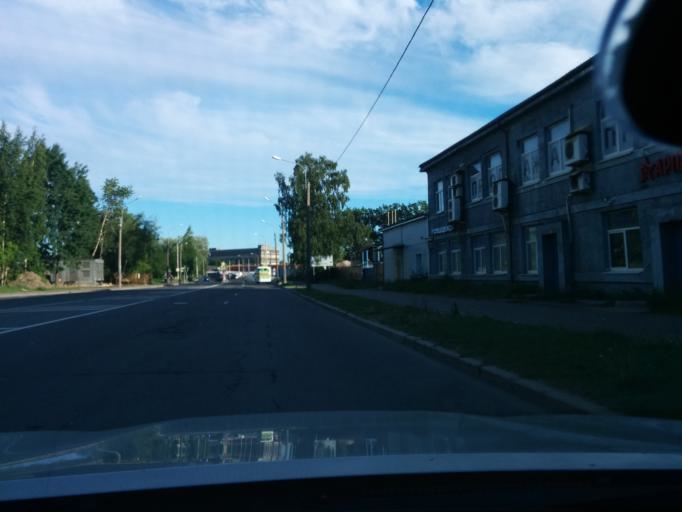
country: RU
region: Leningrad
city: Finlyandskiy
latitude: 59.9791
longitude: 30.3666
